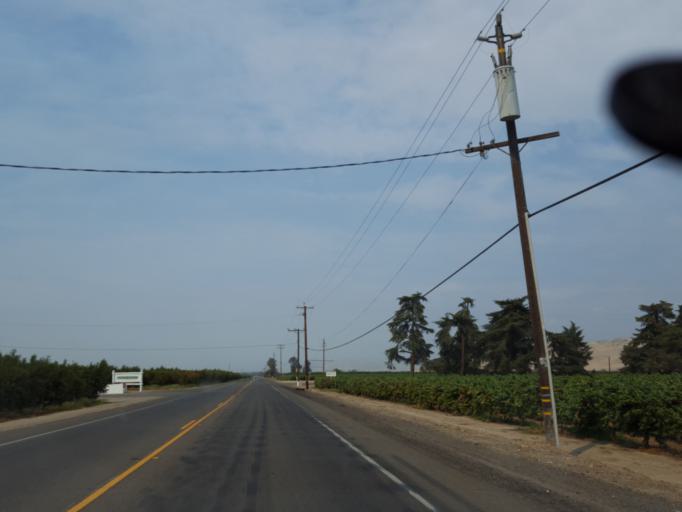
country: US
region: California
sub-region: Fresno County
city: Minkler
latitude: 36.6896
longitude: -119.4574
